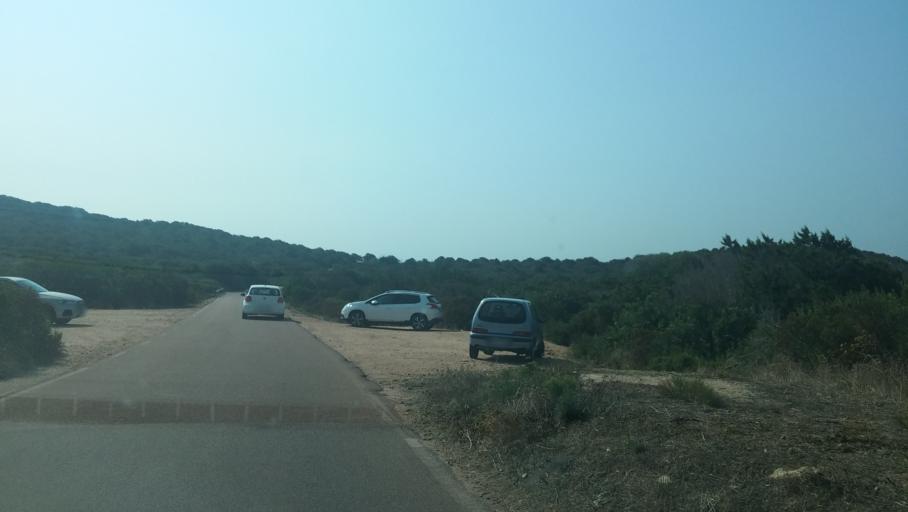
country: IT
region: Sardinia
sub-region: Provincia di Olbia-Tempio
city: La Maddalena
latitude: 41.1886
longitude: 9.4561
